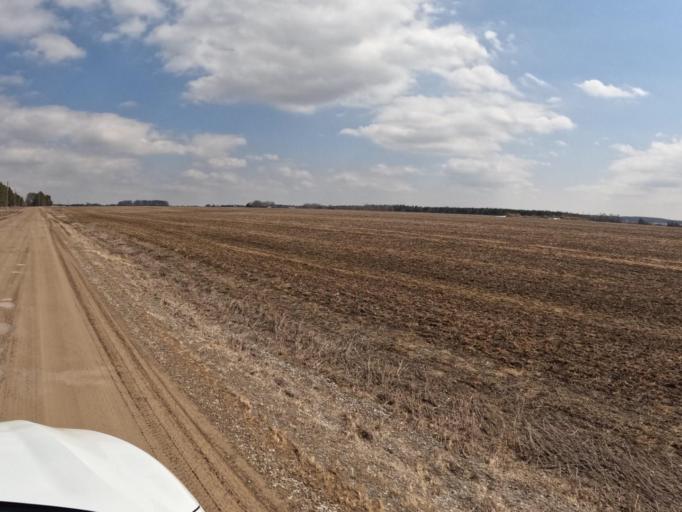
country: CA
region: Ontario
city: Shelburne
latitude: 44.0624
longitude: -80.2324
